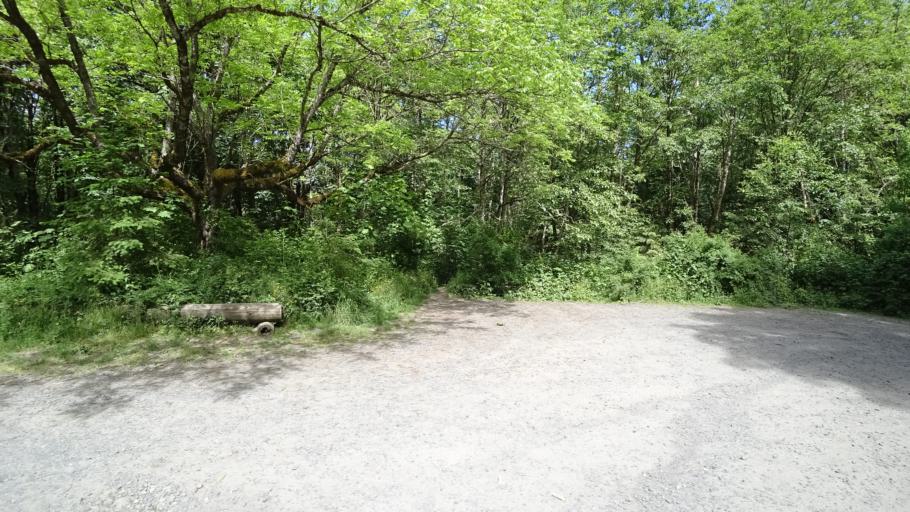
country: US
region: Oregon
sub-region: Washington County
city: Oak Hills
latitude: 45.5916
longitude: -122.8023
